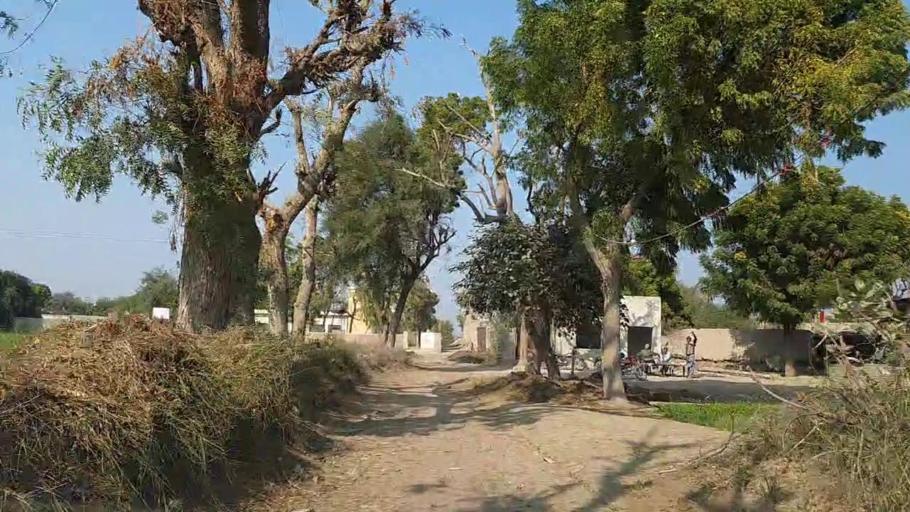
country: PK
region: Sindh
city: Moro
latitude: 26.6845
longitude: 67.9461
